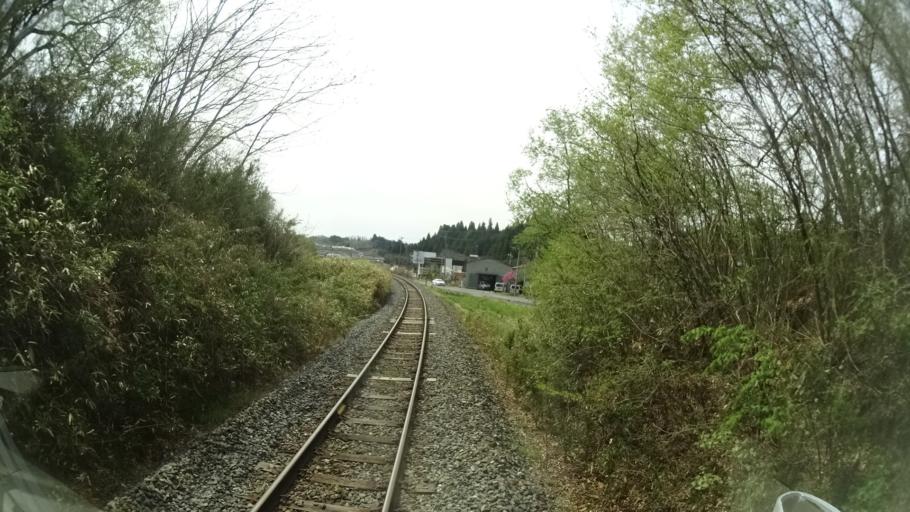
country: JP
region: Iwate
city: Ichinoseki
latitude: 38.9271
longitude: 141.3398
